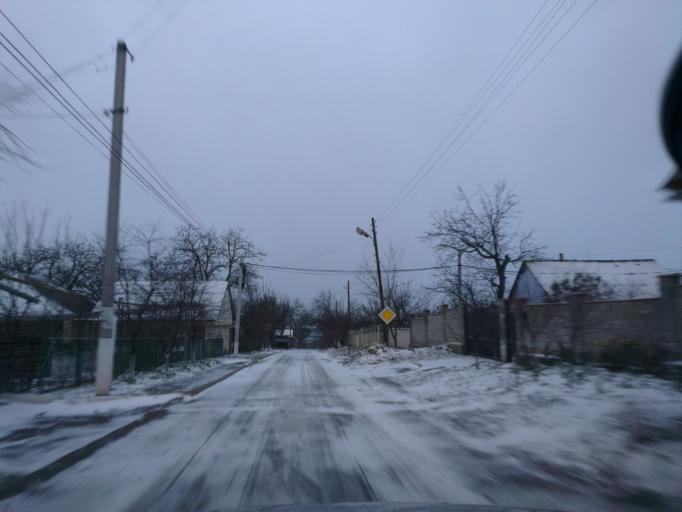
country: MD
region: Chisinau
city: Ciorescu
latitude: 47.1158
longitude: 28.9023
